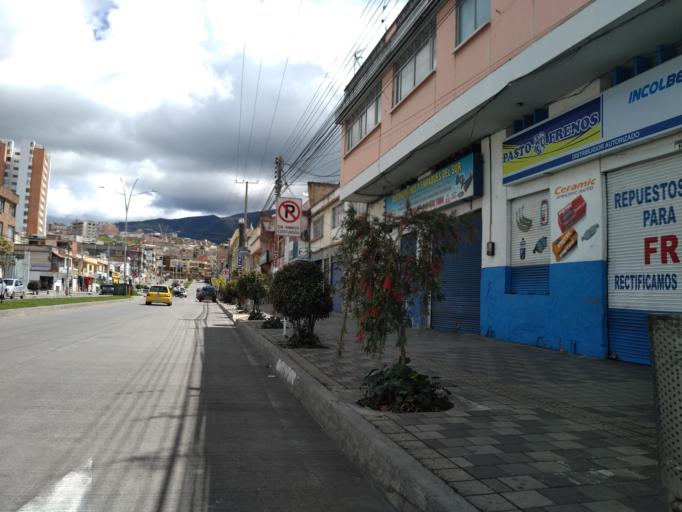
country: CO
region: Narino
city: Pasto
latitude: 1.2075
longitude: -77.2788
